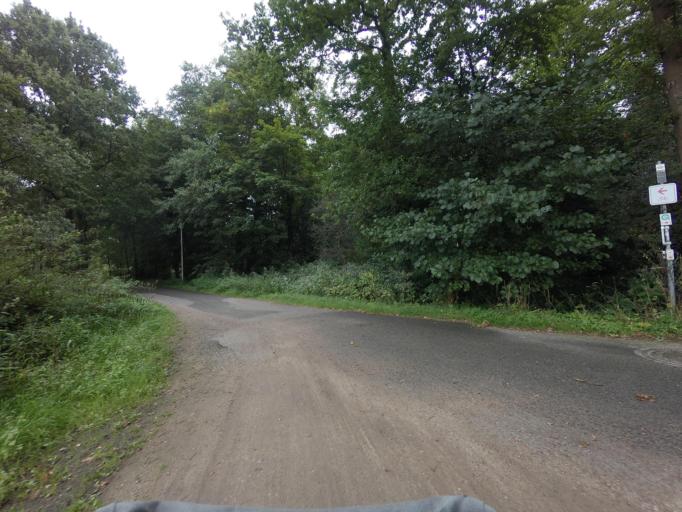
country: DE
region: North Rhine-Westphalia
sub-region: Regierungsbezirk Munster
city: Gronau
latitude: 52.2242
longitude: 7.0298
